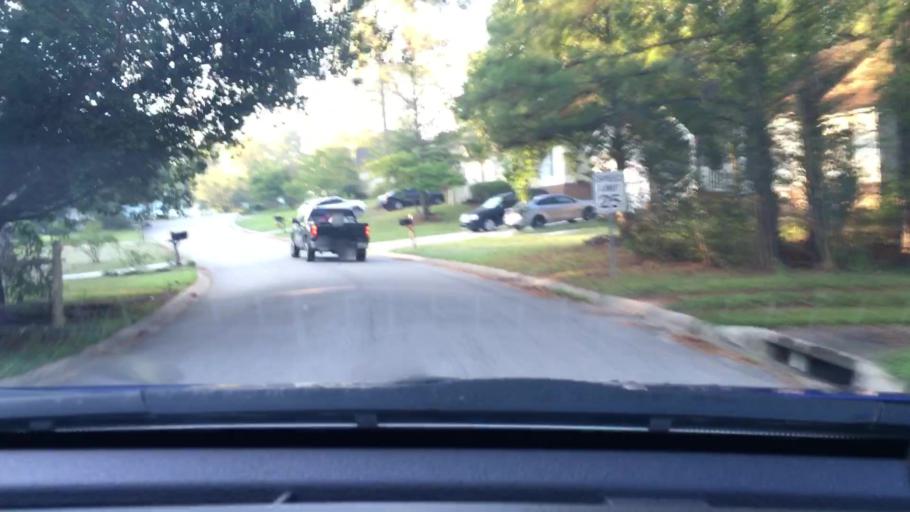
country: US
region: South Carolina
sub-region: Lexington County
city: Irmo
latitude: 34.1027
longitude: -81.1553
